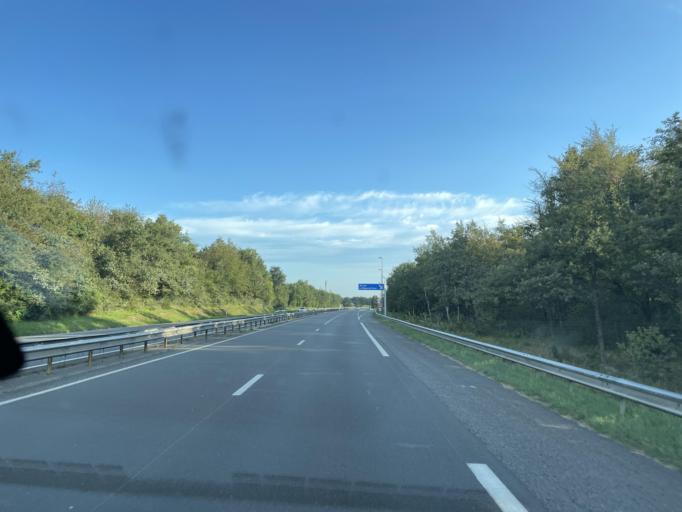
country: FR
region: Rhone-Alpes
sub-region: Departement de la Loire
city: Montrond-les-Bains
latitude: 45.6751
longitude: 4.1565
